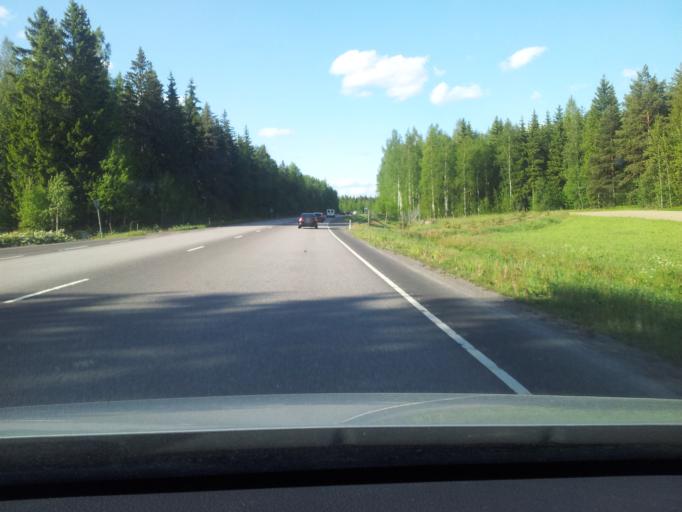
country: FI
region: Uusimaa
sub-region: Loviisa
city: Lapinjaervi
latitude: 60.6771
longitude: 26.2554
